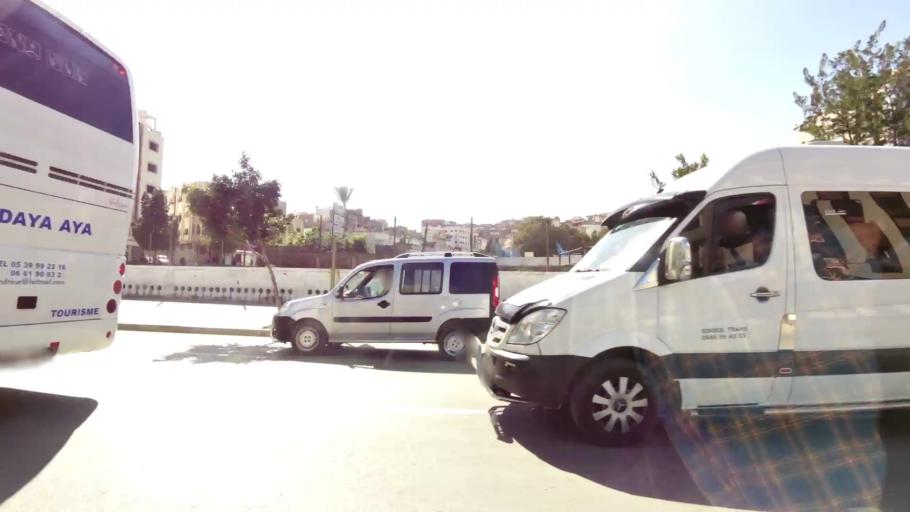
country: MA
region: Tanger-Tetouan
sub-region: Tanger-Assilah
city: Tangier
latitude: 35.7420
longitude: -5.8061
